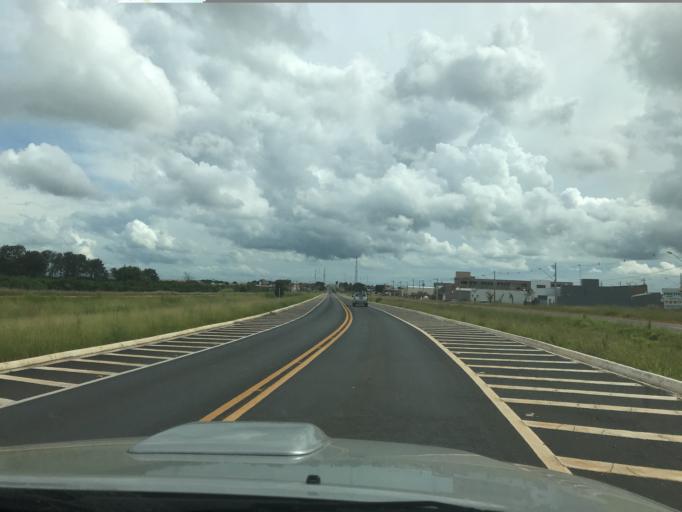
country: BR
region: Minas Gerais
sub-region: Patrocinio
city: Patrocinio
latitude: -19.1000
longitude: -46.6760
